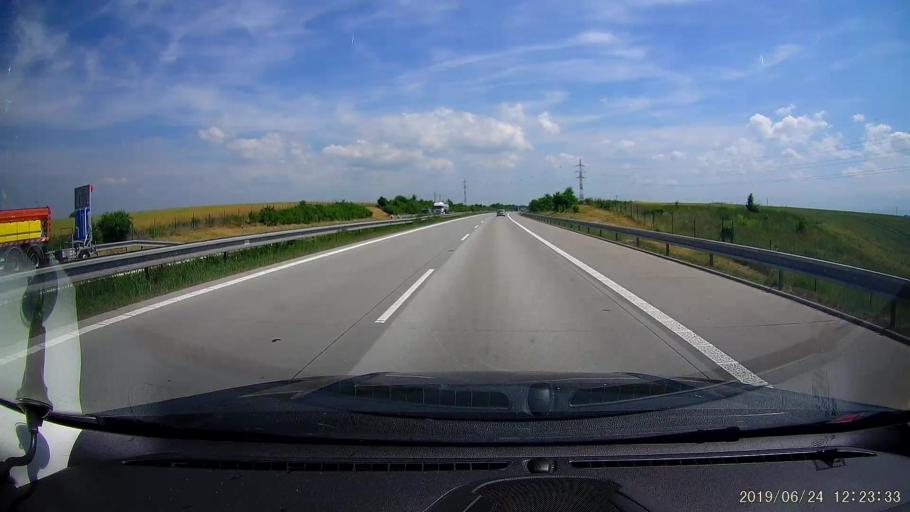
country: CZ
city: Bilovec
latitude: 49.7350
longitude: 18.0320
